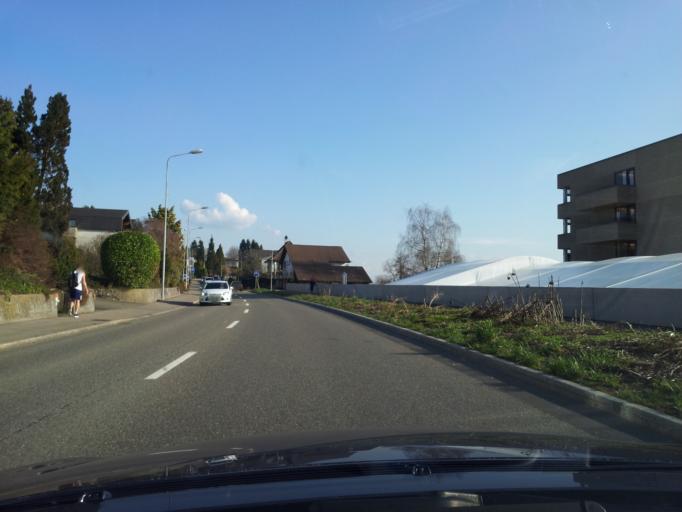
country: CH
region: Aargau
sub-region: Bezirk Baden
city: Kunten
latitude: 47.3883
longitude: 8.3442
